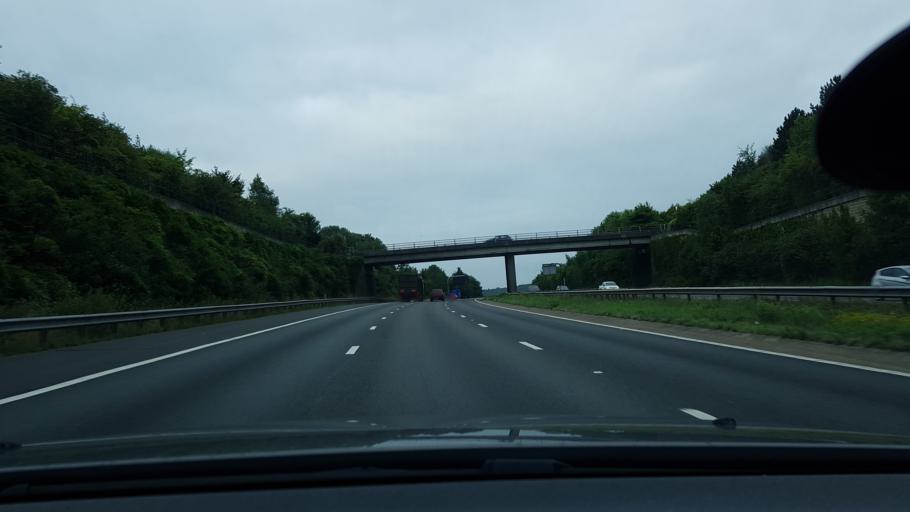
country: GB
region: England
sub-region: Hampshire
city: Compton
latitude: 51.0220
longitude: -1.3340
